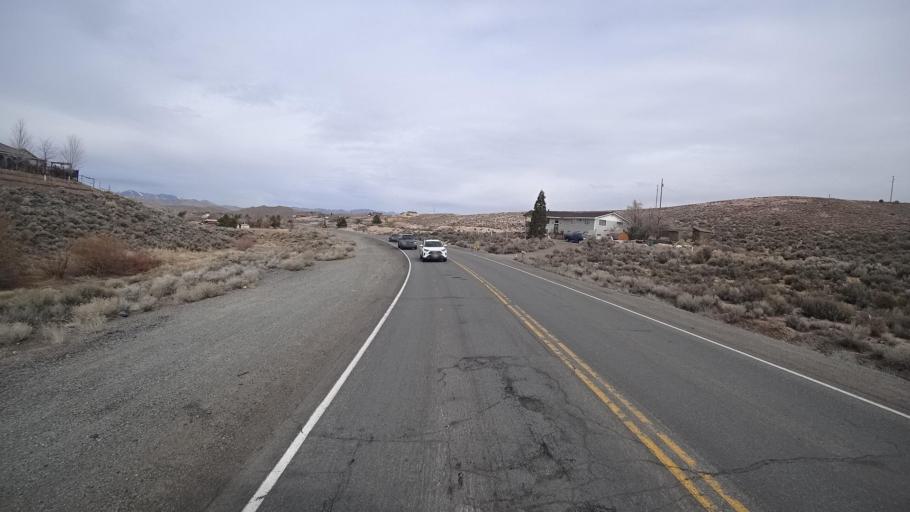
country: US
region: Nevada
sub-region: Washoe County
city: Golden Valley
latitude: 39.6052
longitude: -119.8096
